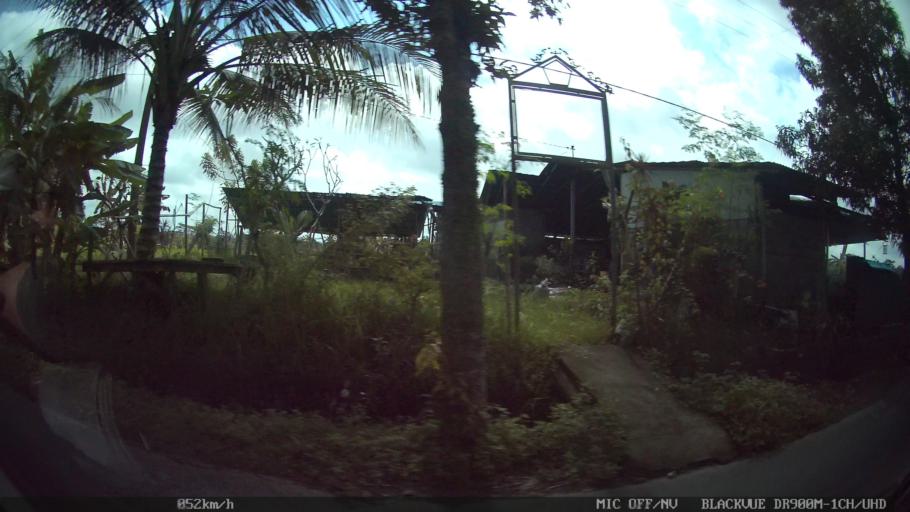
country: ID
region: Bali
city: Banjar Mulung
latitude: -8.5046
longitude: 115.3209
